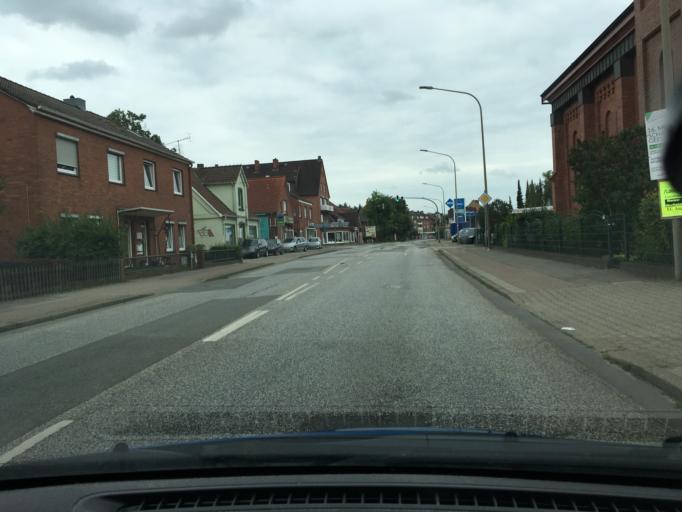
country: DE
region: Schleswig-Holstein
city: Geesthacht
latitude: 53.4412
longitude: 10.3653
